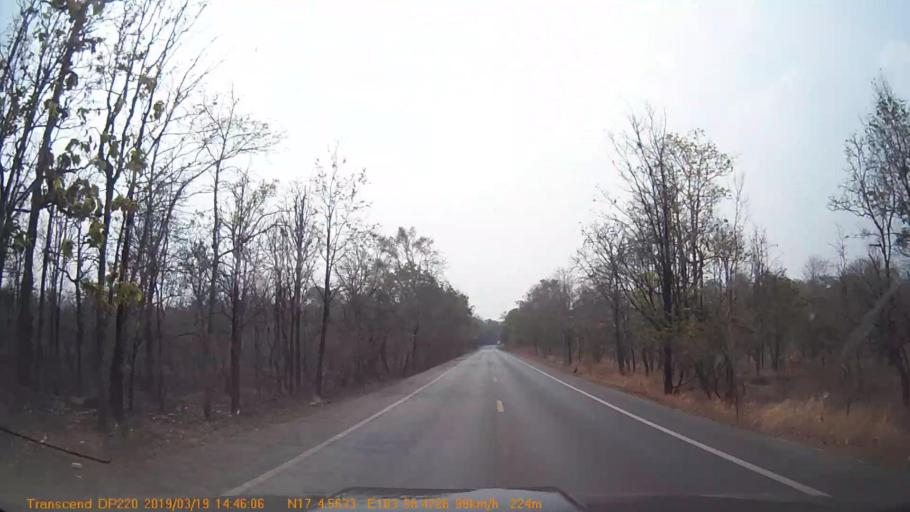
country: TH
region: Sakon Nakhon
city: Phu Phan
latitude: 17.0762
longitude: 103.9409
